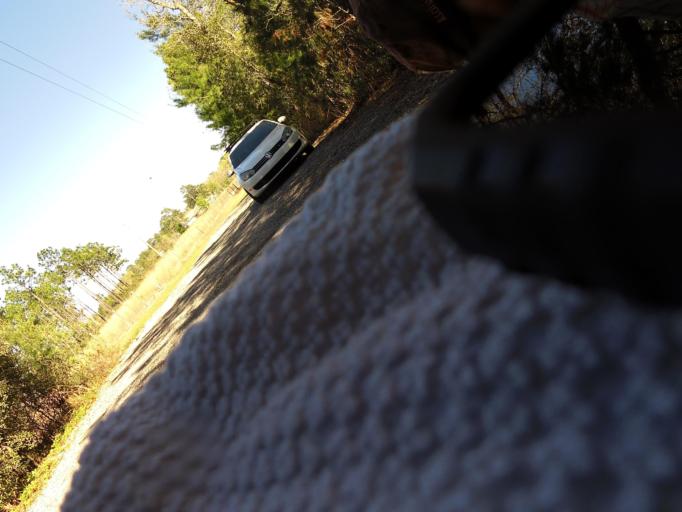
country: US
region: Florida
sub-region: Clay County
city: Keystone Heights
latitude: 29.8133
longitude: -82.0055
